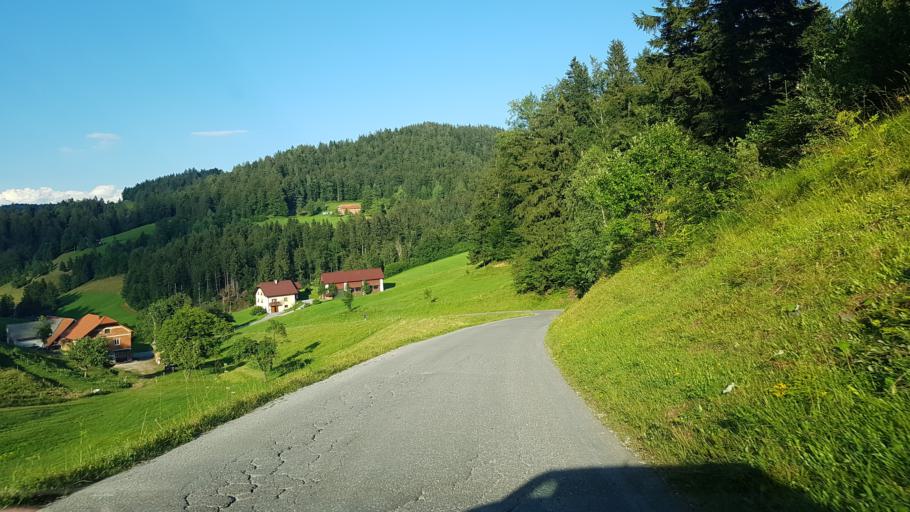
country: SI
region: Idrija
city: Spodnja Idrija
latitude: 46.0725
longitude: 14.0215
